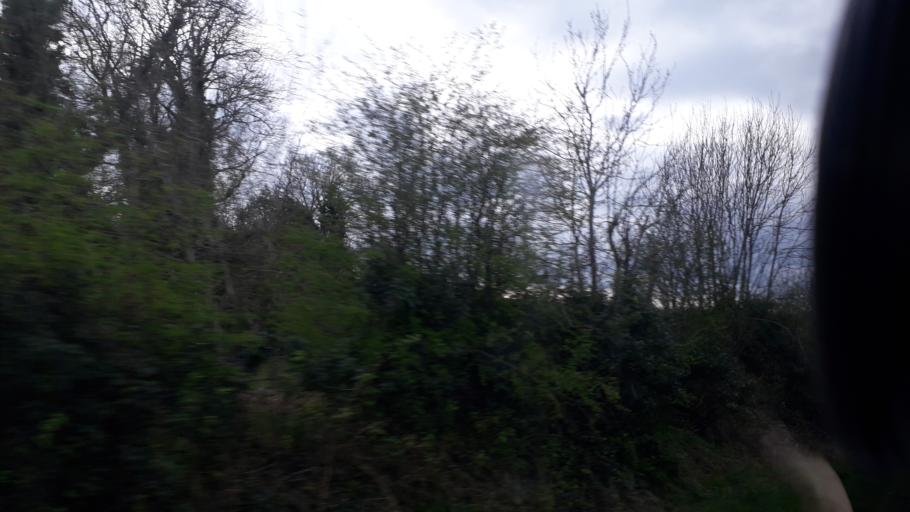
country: IE
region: Leinster
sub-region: An Longfort
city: Longford
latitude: 53.7070
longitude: -7.7185
